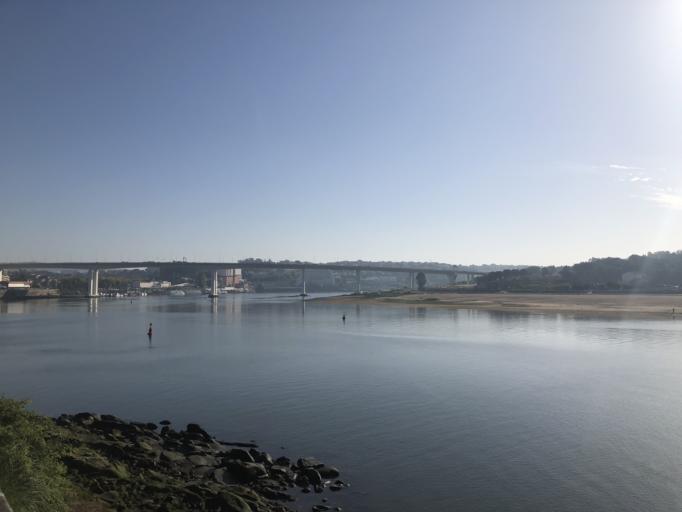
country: PT
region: Porto
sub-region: Vila Nova de Gaia
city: Oliveira do Douro
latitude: 41.1405
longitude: -8.5896
